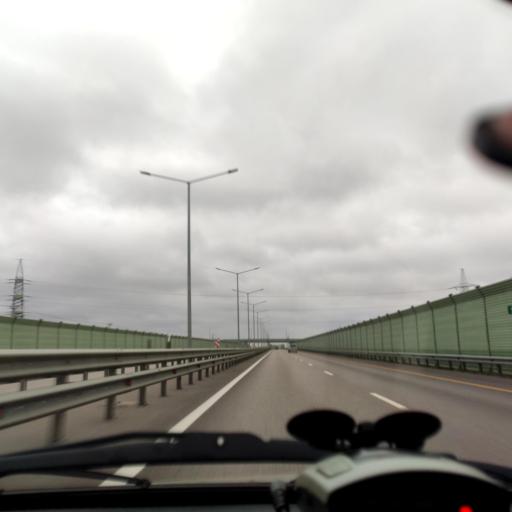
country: RU
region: Voronezj
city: Novaya Usman'
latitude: 51.6182
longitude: 39.3189
